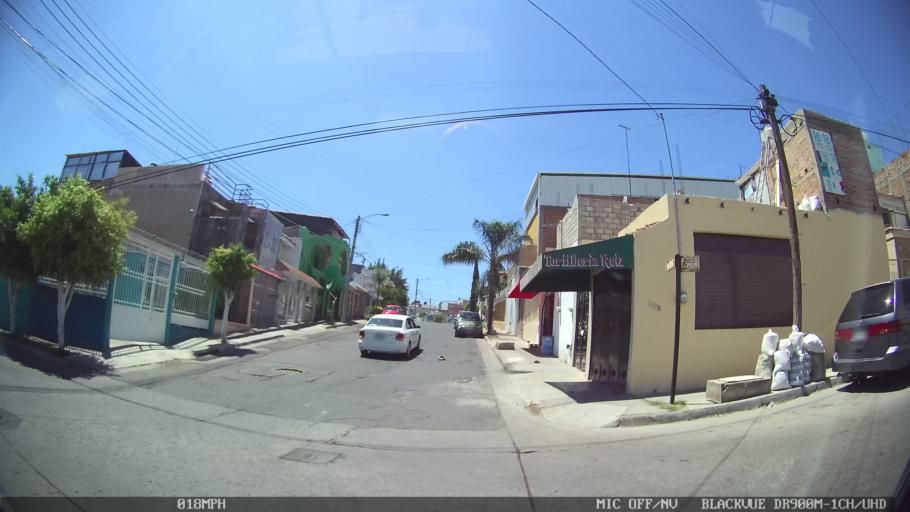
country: MX
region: Jalisco
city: Tlaquepaque
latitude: 20.6818
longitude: -103.2900
